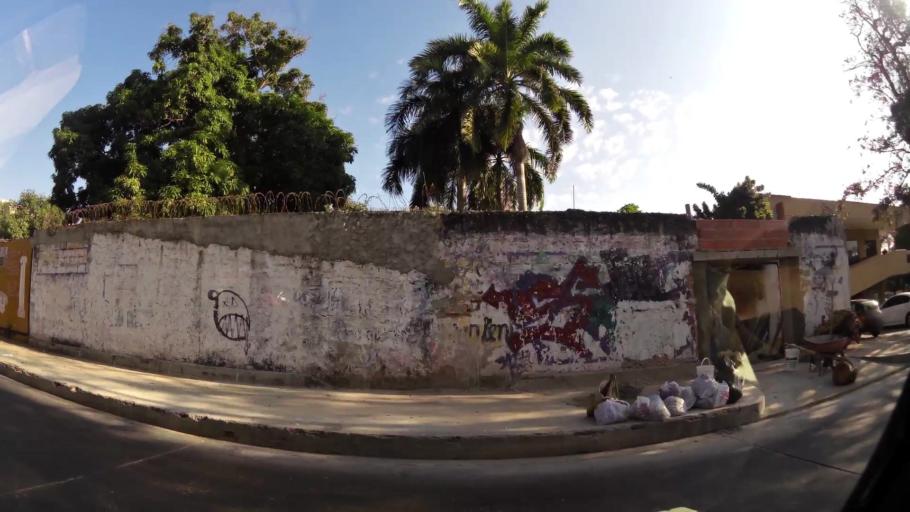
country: CO
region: Atlantico
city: Barranquilla
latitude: 10.9962
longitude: -74.8022
